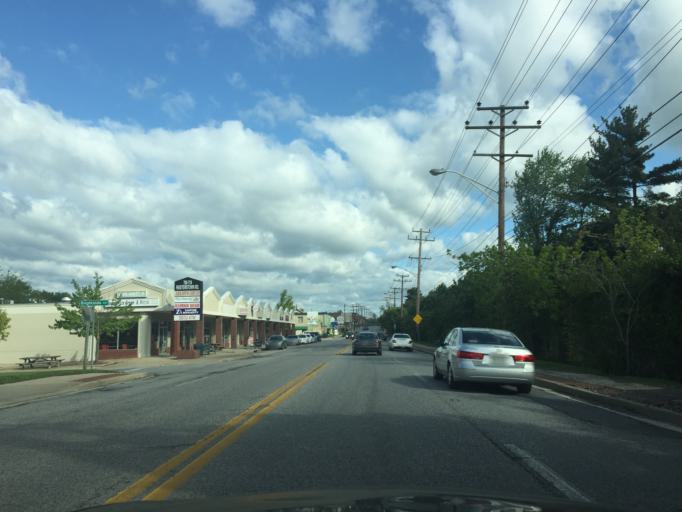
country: US
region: Maryland
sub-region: Baltimore County
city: Pikesville
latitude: 39.3706
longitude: -76.7193
